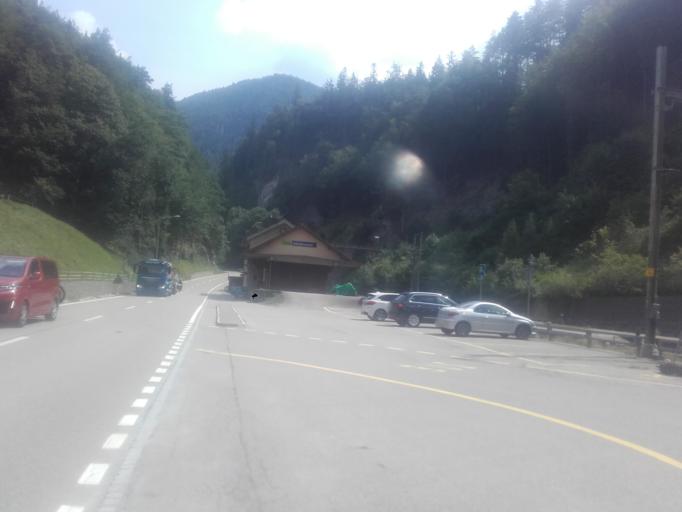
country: CH
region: Solothurn
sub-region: Bezirk Lebern
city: Selzach
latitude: 47.2662
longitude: 7.4645
